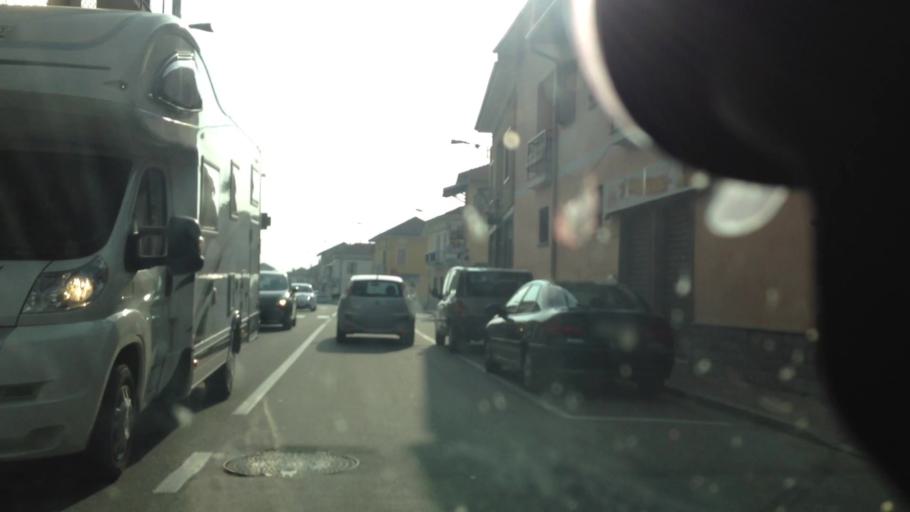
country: IT
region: Piedmont
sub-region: Provincia di Vercelli
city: Borgo d'Ale
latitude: 45.3482
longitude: 8.0521
